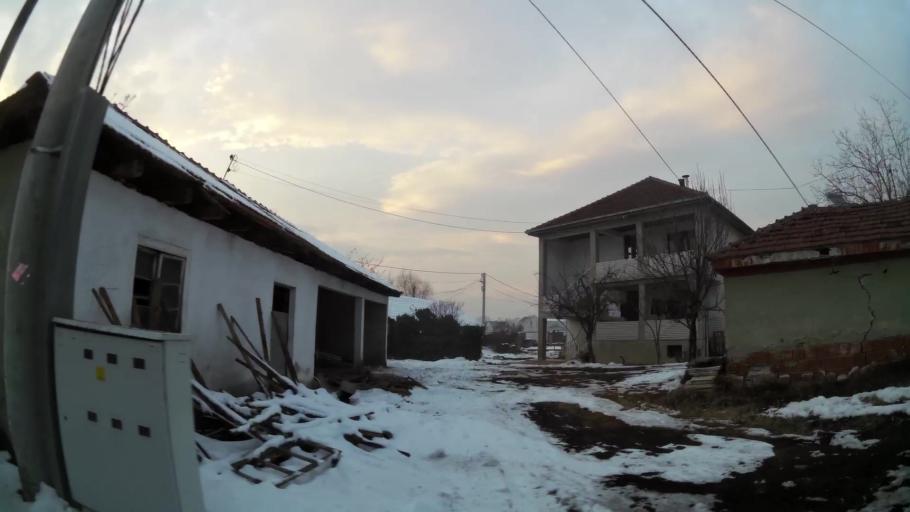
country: MK
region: Suto Orizari
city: Suto Orizare
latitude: 42.0361
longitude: 21.4085
